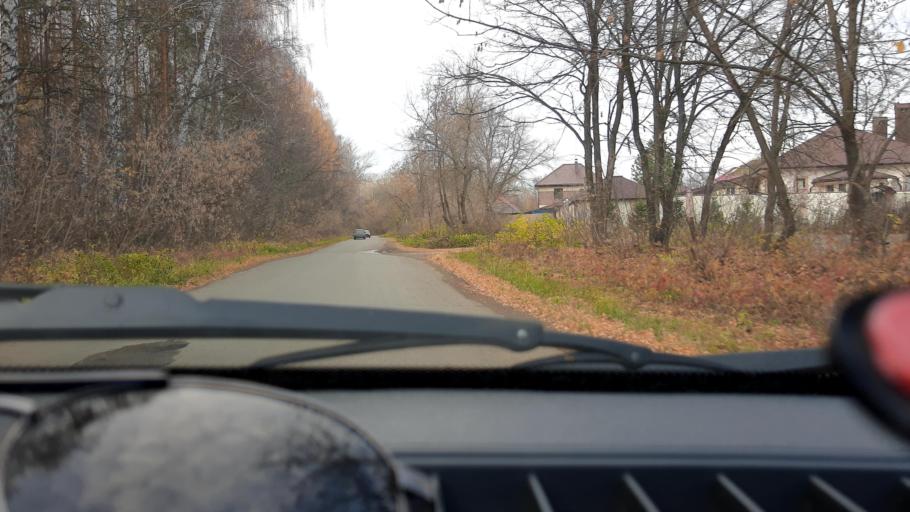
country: RU
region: Bashkortostan
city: Ufa
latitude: 54.7898
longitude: 56.1582
